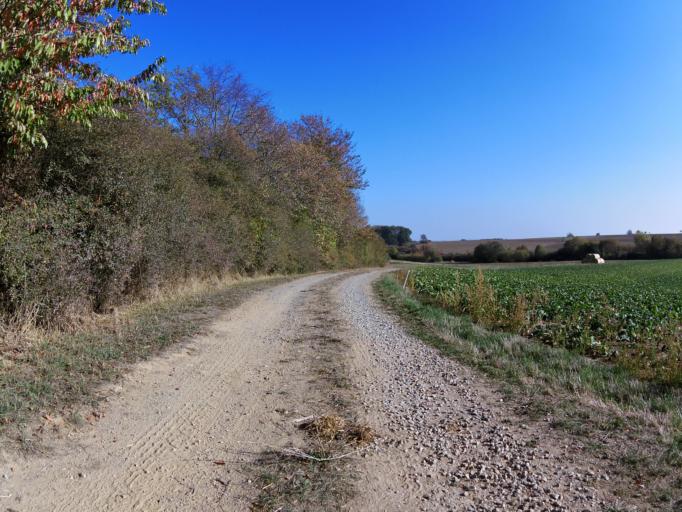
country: DE
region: Bavaria
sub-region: Regierungsbezirk Unterfranken
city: Geroldshausen
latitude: 49.6971
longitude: 9.9104
